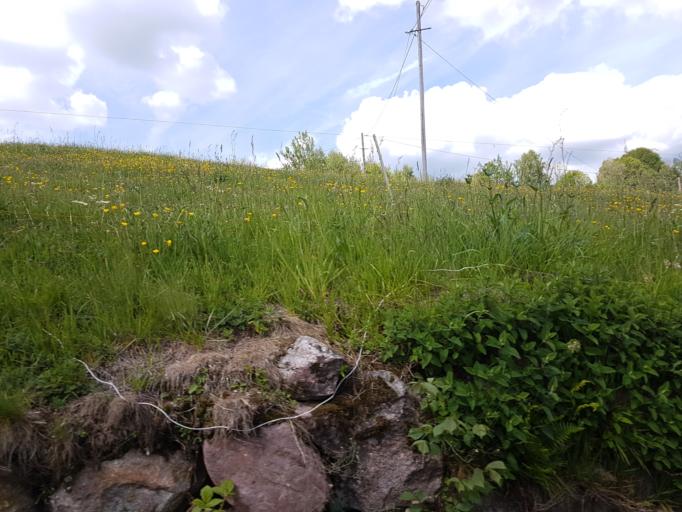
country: FR
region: Lorraine
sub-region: Departement des Vosges
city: Rupt-sur-Moselle
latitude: 47.8674
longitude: 6.6756
